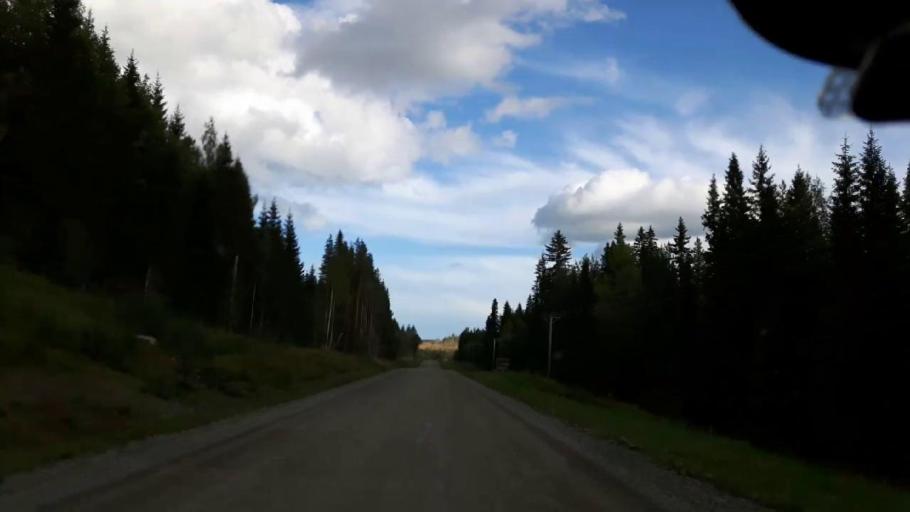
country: SE
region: Jaemtland
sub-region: Stroemsunds Kommun
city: Stroemsund
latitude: 63.3007
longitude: 15.5795
